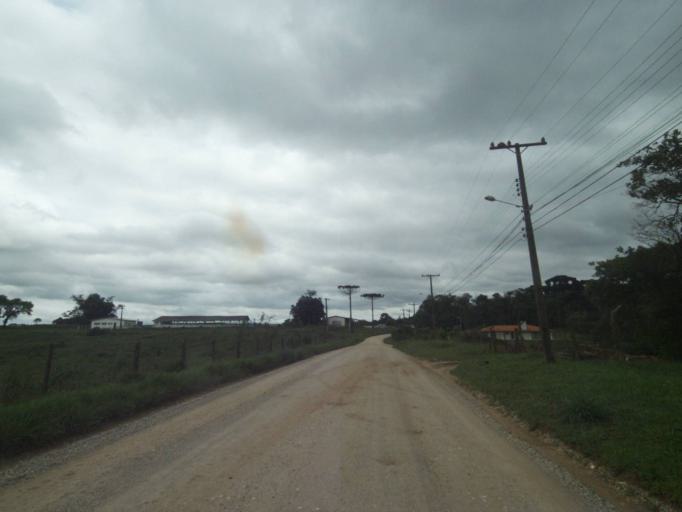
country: BR
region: Parana
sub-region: Campina Grande Do Sul
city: Campina Grande do Sul
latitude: -25.3250
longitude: -49.0880
